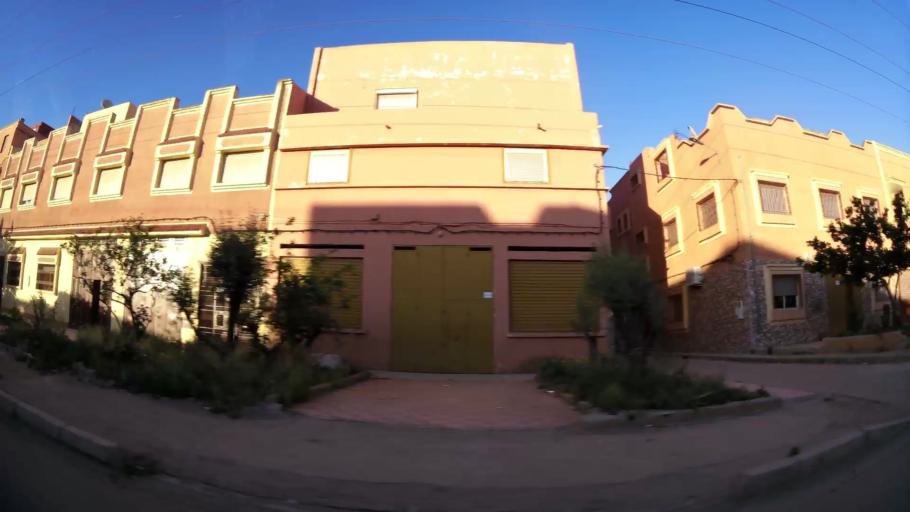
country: MA
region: Oriental
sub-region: Berkane-Taourirt
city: Berkane
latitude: 34.9242
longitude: -2.3128
